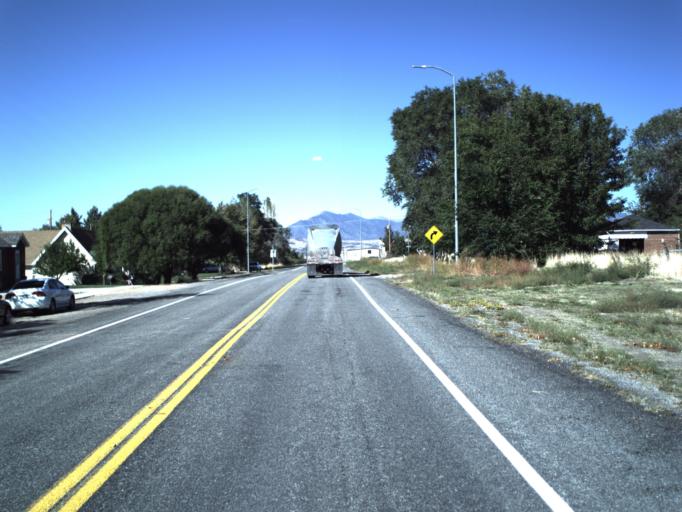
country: US
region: Utah
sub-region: Millard County
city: Fillmore
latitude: 39.1031
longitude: -112.2709
